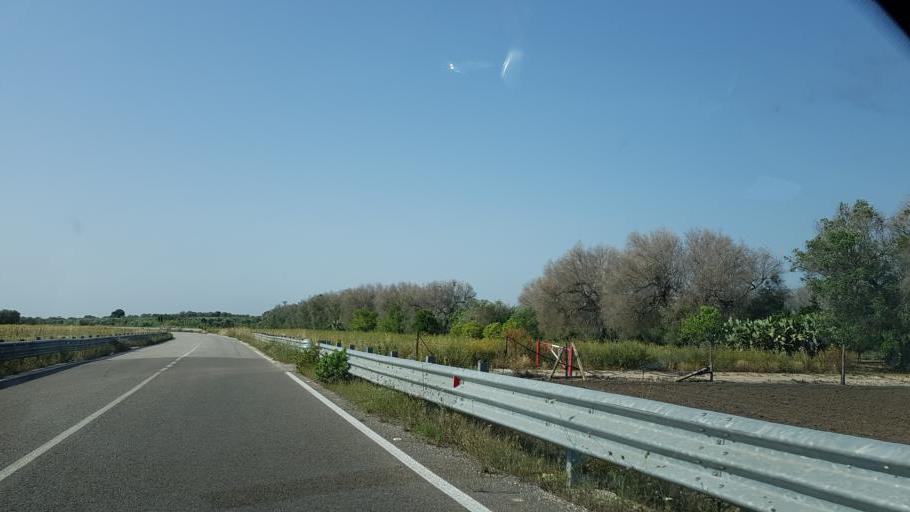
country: IT
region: Apulia
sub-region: Provincia di Brindisi
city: Mesagne
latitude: 40.4983
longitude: 17.8290
